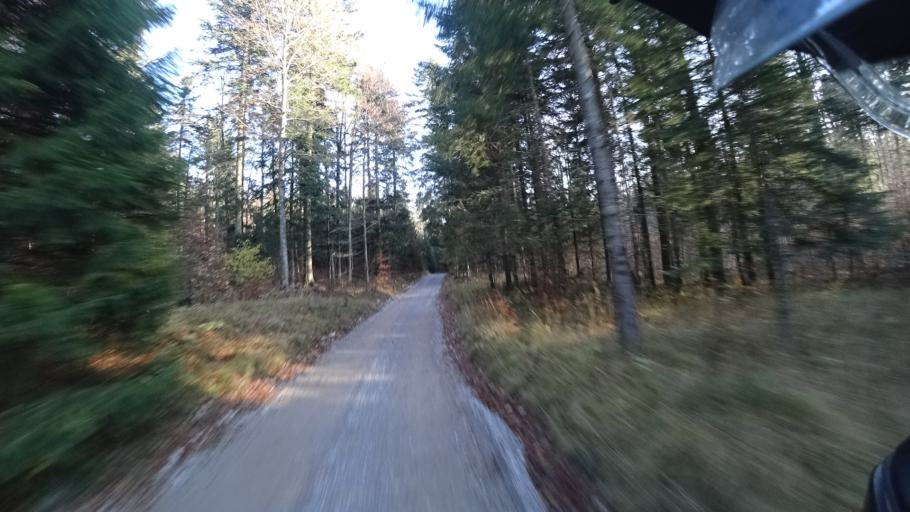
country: HR
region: Primorsko-Goranska
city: Drazice
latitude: 45.4813
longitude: 14.4734
